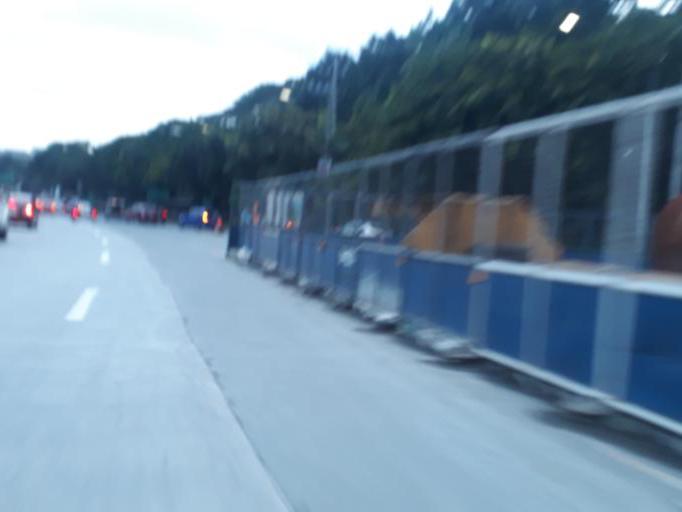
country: PH
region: Metro Manila
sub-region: Quezon City
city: Quezon City
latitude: 14.6520
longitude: 121.0465
